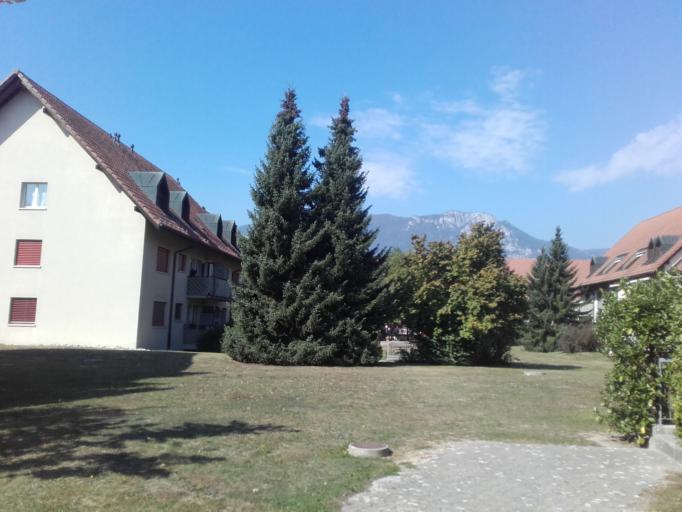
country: CH
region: Solothurn
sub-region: Bezirk Wasseramt
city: Zuchwil
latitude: 47.2138
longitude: 7.5629
